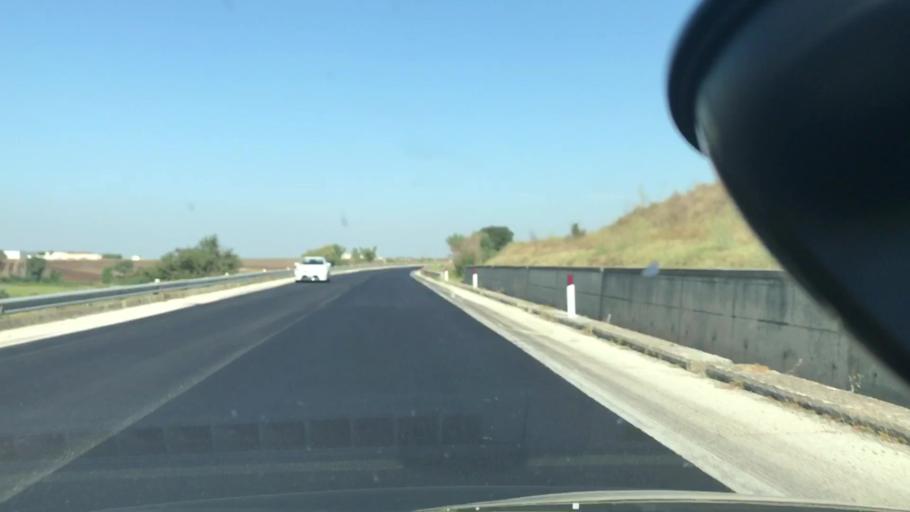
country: IT
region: Apulia
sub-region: Provincia di Barletta - Andria - Trani
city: Spinazzola
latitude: 40.9069
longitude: 16.1103
